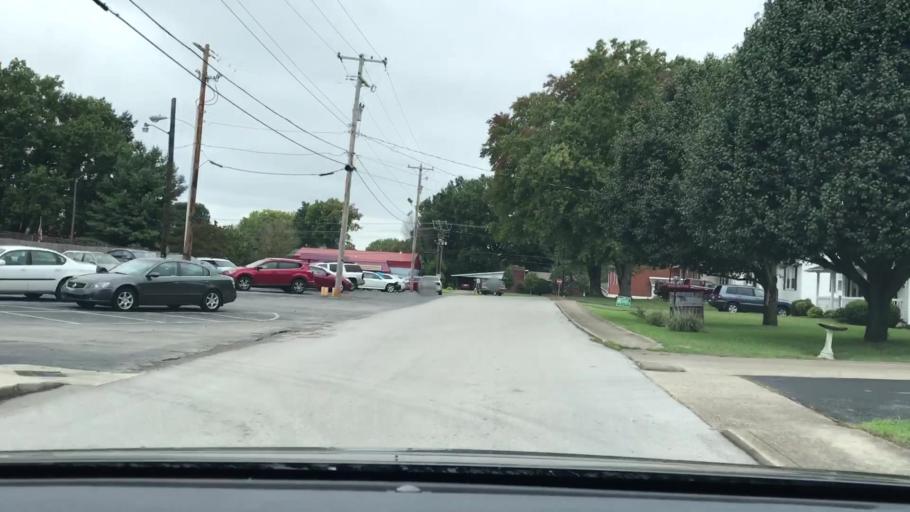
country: US
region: Kentucky
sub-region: Pulaski County
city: Somerset
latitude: 37.0855
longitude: -84.5977
